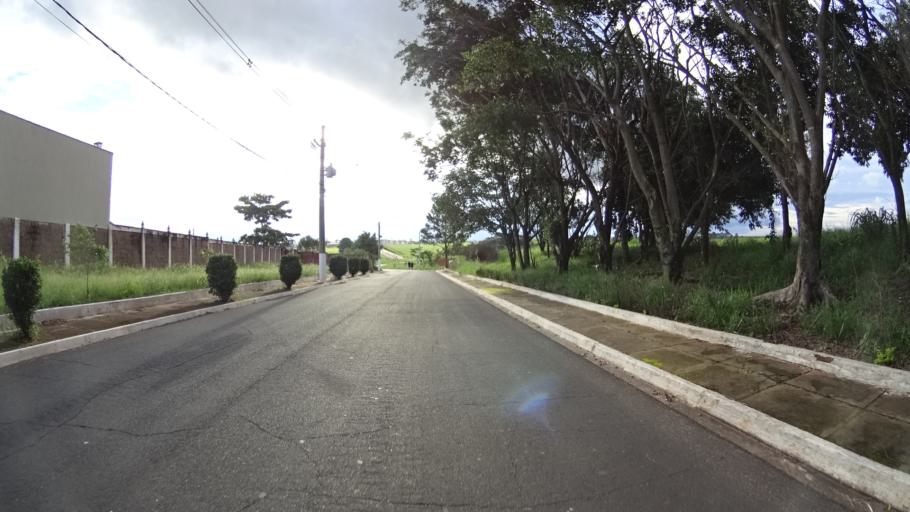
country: BR
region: Sao Paulo
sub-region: Marilia
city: Marilia
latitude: -22.2226
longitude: -49.8917
